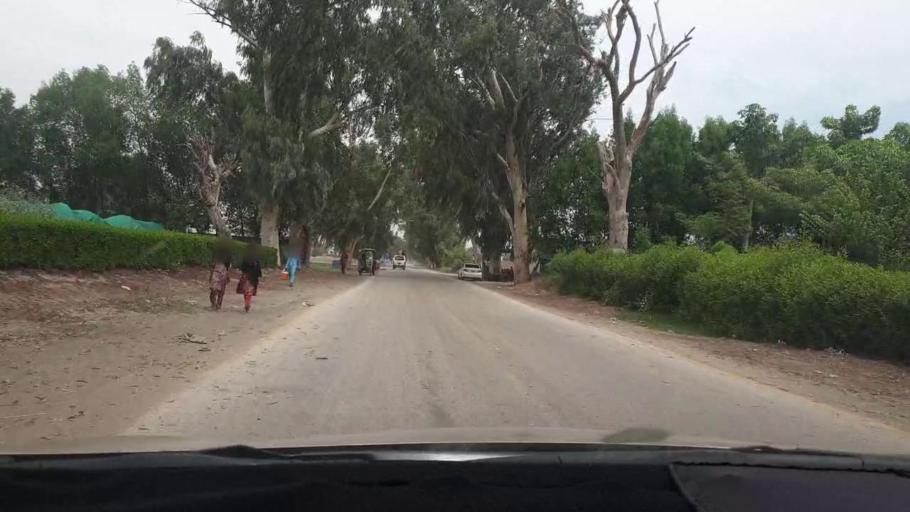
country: PK
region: Sindh
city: Naudero
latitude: 27.6584
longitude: 68.3452
